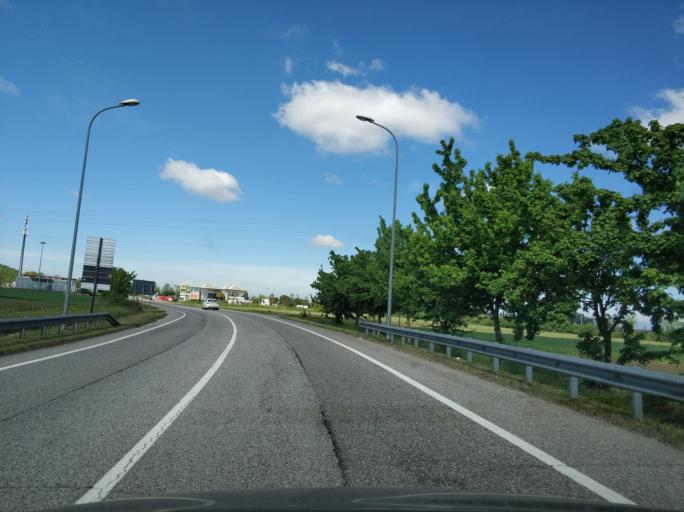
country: IT
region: Veneto
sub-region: Provincia di Venezia
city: Arino
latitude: 45.4463
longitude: 12.0460
